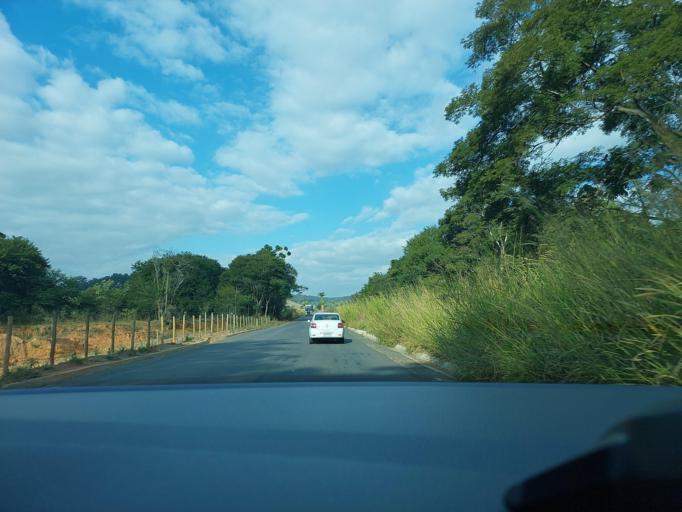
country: BR
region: Minas Gerais
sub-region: Vicosa
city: Vicosa
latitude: -20.8266
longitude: -42.7698
